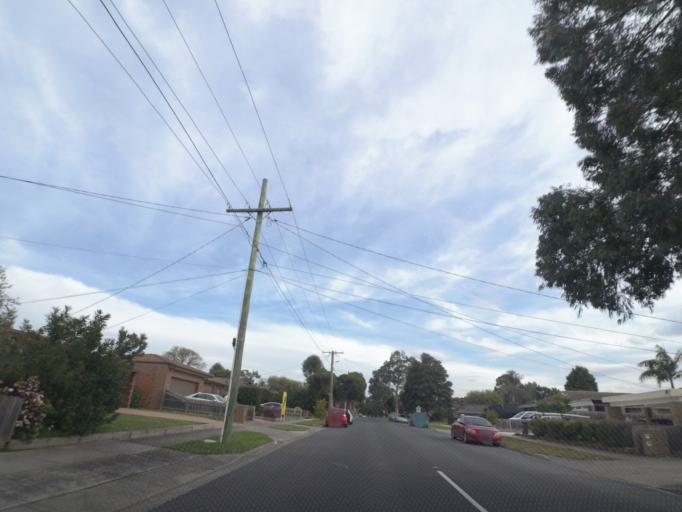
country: AU
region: Victoria
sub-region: Knox
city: Knoxfield
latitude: -37.8833
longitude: 145.2615
